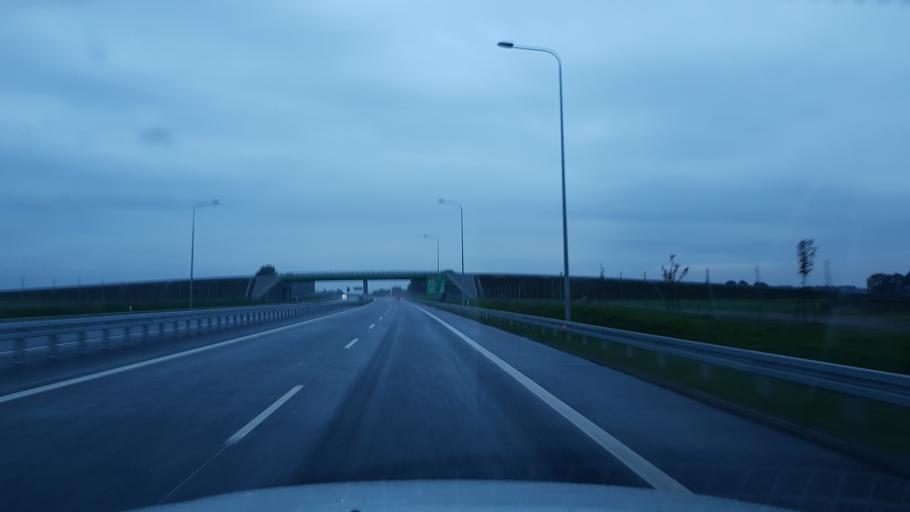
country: PL
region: West Pomeranian Voivodeship
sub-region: Powiat gryficki
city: Brojce
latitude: 53.8822
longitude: 15.3782
